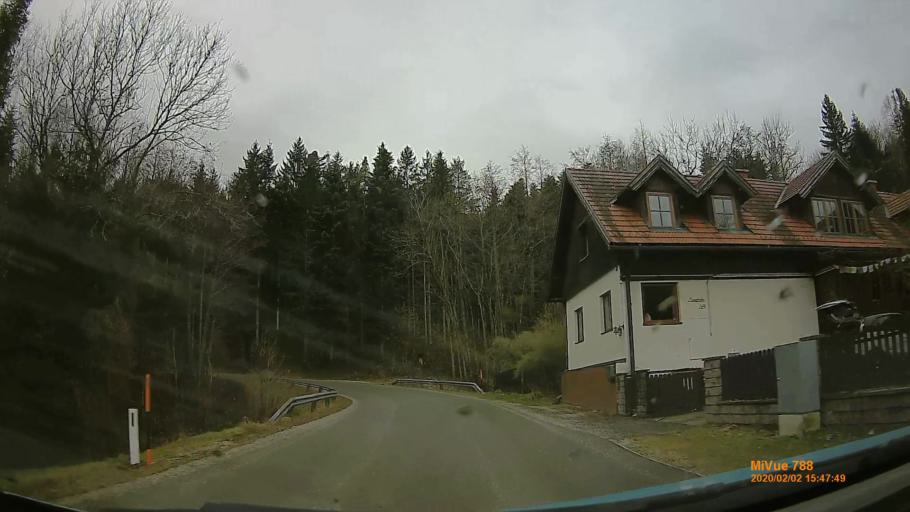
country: AT
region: Lower Austria
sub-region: Politischer Bezirk Neunkirchen
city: Reichenau an der Rax
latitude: 47.6867
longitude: 15.8155
